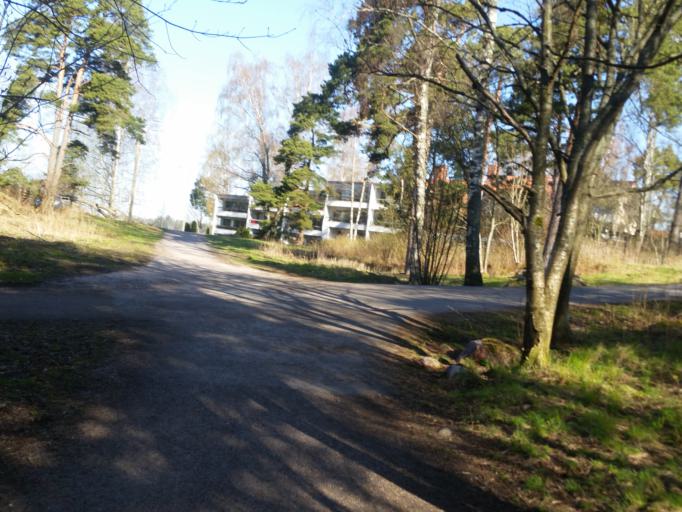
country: FI
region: Uusimaa
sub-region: Helsinki
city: Helsinki
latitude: 60.1466
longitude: 24.8788
